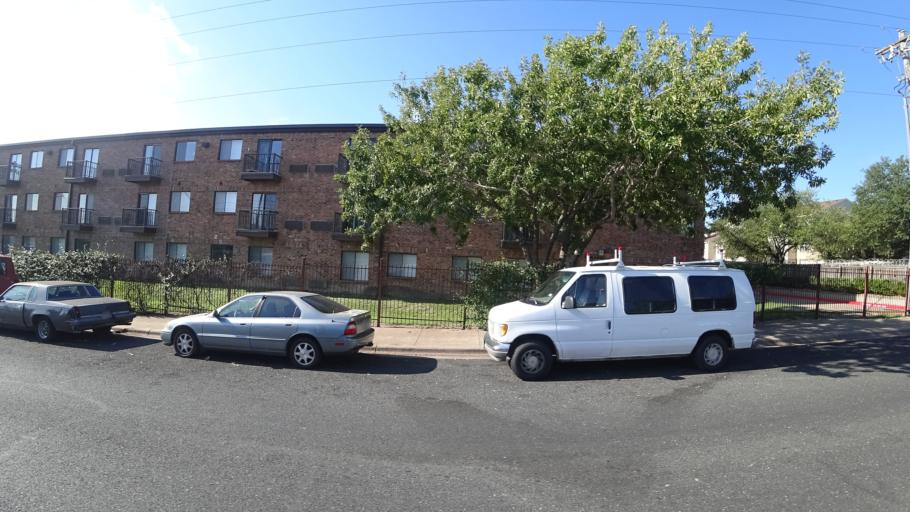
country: US
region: Texas
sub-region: Travis County
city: Austin
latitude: 30.3252
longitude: -97.6962
